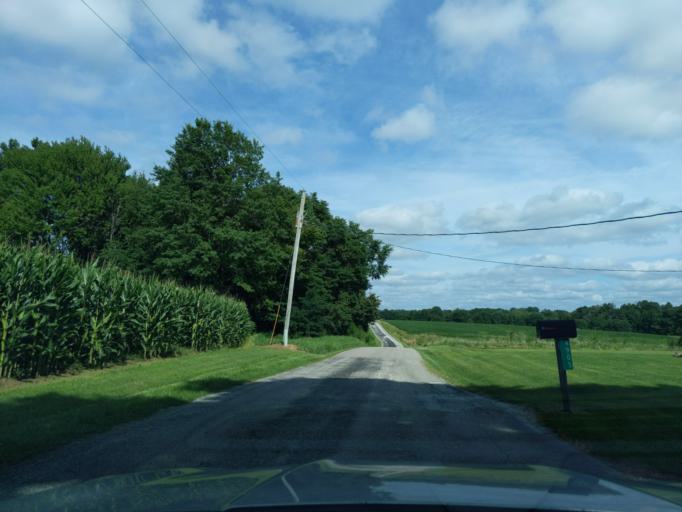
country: US
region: Indiana
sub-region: Decatur County
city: Greensburg
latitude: 39.2349
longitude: -85.3862
